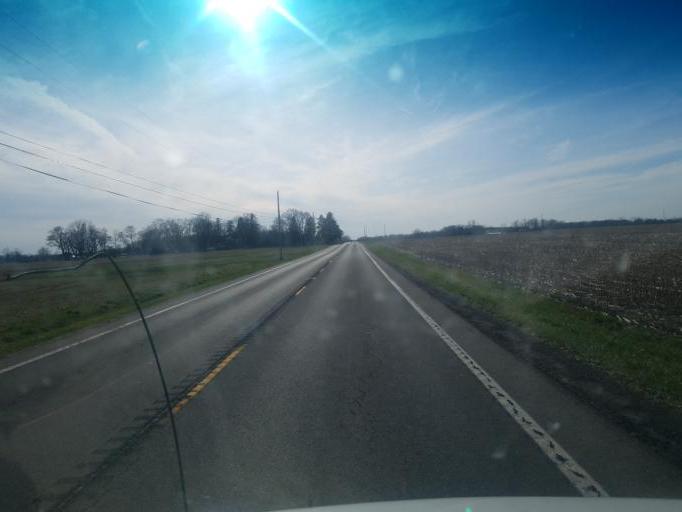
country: US
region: Ohio
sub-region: Logan County
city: Bellefontaine
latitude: 40.3655
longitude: -83.8310
